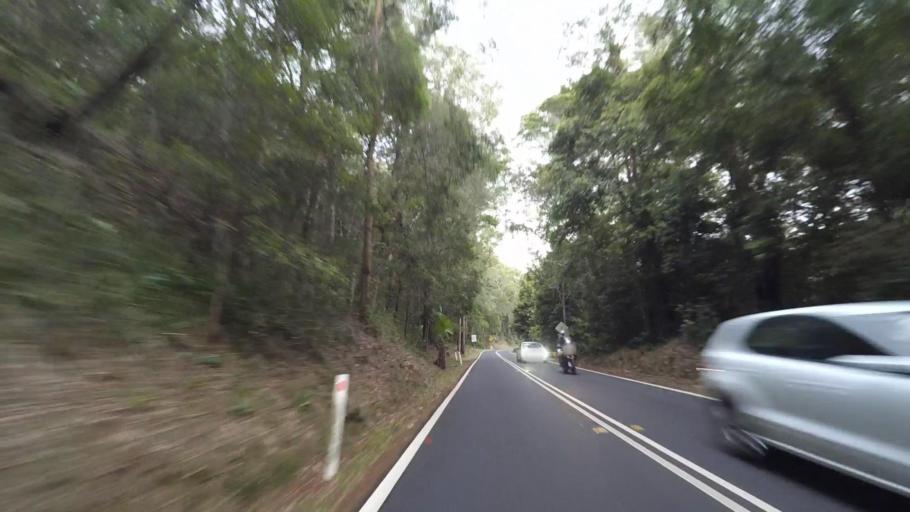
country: AU
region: New South Wales
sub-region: Wollongong
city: Helensburgh
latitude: -34.1563
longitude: 151.0289
